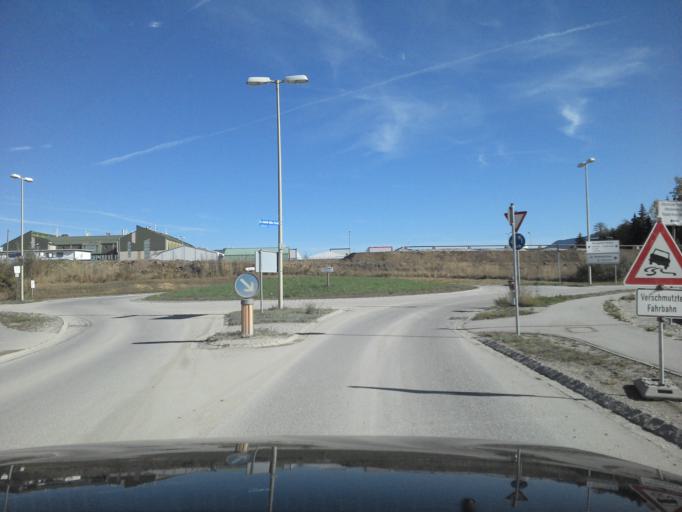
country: DE
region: Bavaria
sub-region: Upper Bavaria
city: Penzberg
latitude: 47.7716
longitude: 11.3699
